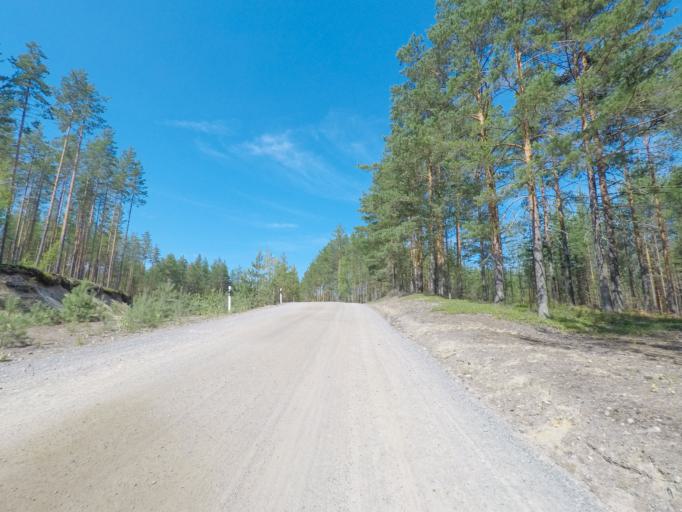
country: FI
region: Southern Savonia
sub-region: Mikkeli
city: Puumala
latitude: 61.4233
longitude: 28.0387
